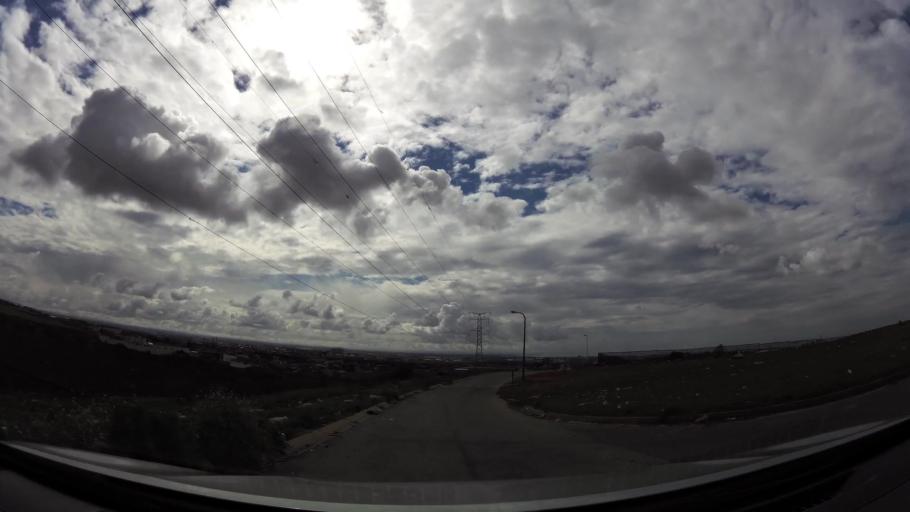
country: ZA
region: Eastern Cape
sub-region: Nelson Mandela Bay Metropolitan Municipality
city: Port Elizabeth
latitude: -33.9291
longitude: 25.5600
